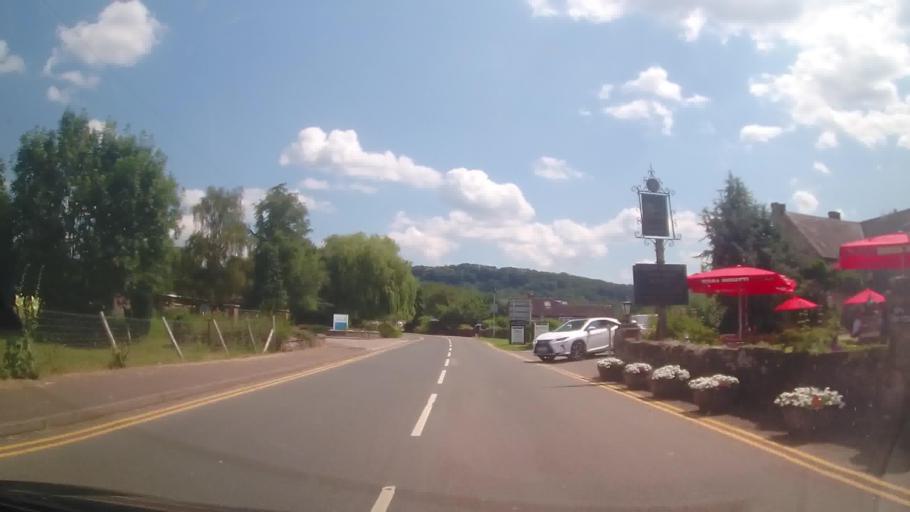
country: GB
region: England
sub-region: Herefordshire
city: Whitchurch
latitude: 51.8540
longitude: -2.6510
